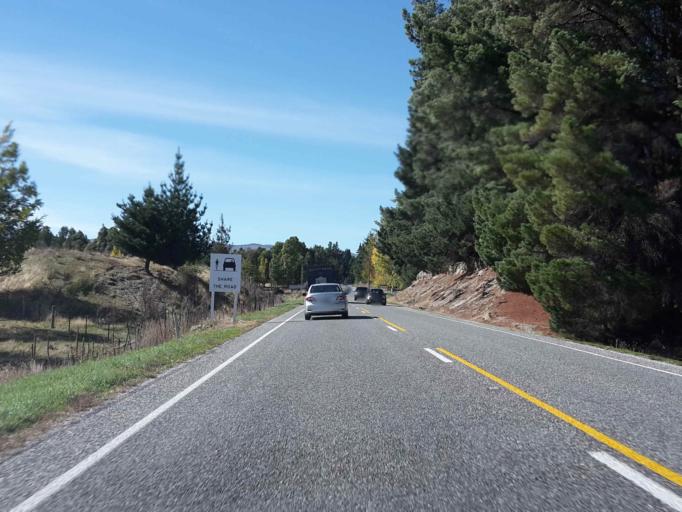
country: NZ
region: Otago
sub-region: Queenstown-Lakes District
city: Wanaka
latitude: -44.7007
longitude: 169.1848
